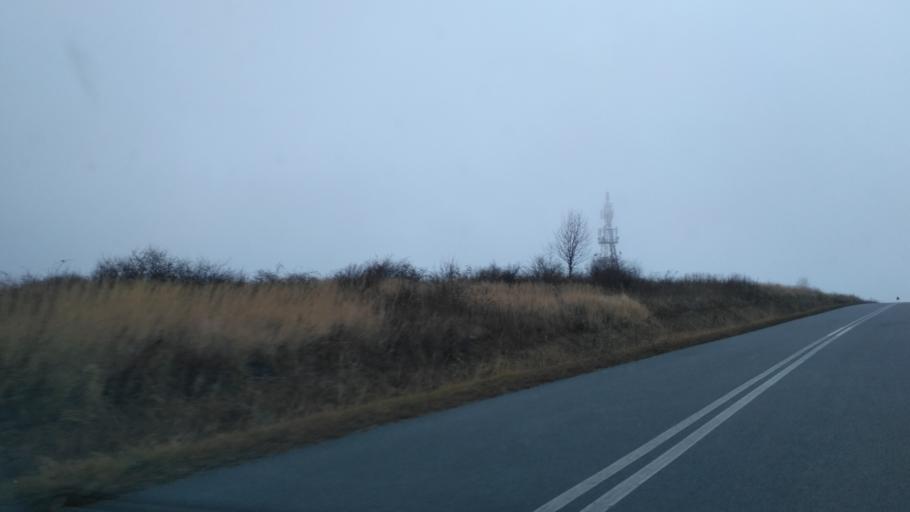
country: PL
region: Subcarpathian Voivodeship
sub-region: Powiat jaroslawski
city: Jodlowka
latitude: 49.8987
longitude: 22.4846
